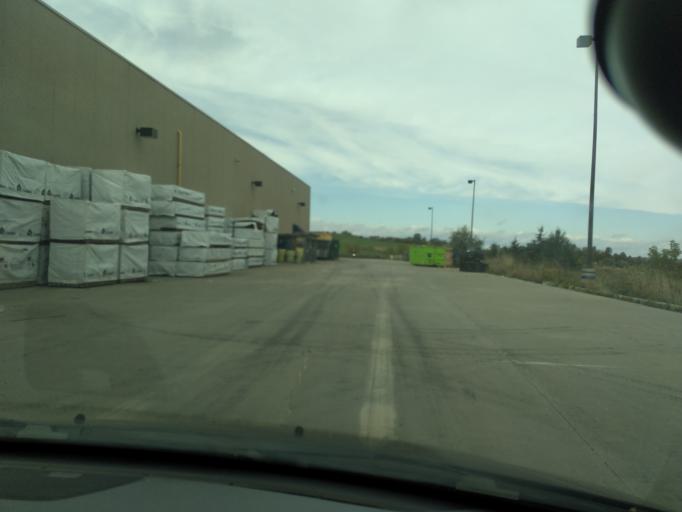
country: CA
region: Ontario
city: Newmarket
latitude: 44.0767
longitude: -79.4801
